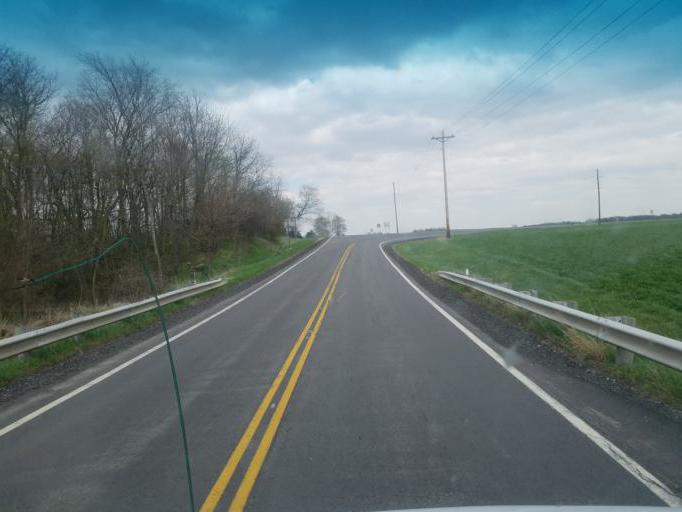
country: US
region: Ohio
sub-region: Crawford County
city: Bucyrus
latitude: 40.9504
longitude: -83.0670
